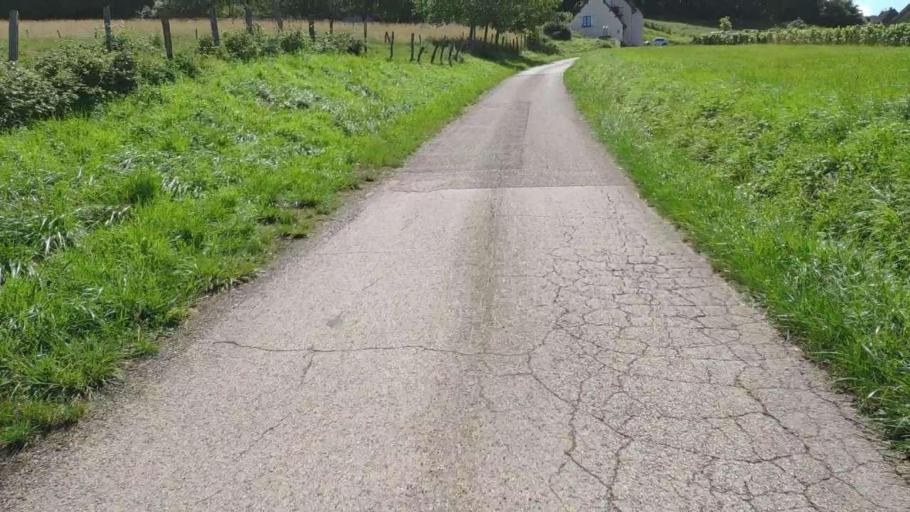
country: FR
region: Franche-Comte
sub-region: Departement du Jura
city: Bletterans
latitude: 46.8041
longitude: 5.5559
